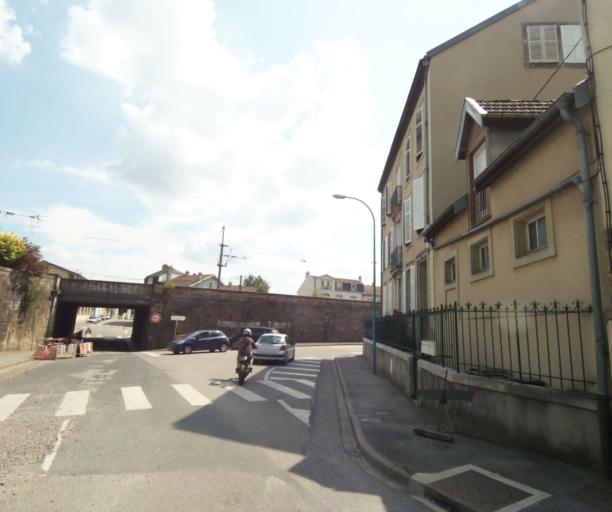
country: FR
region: Lorraine
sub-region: Departement de Meurthe-et-Moselle
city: Luneville
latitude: 48.5876
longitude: 6.4935
